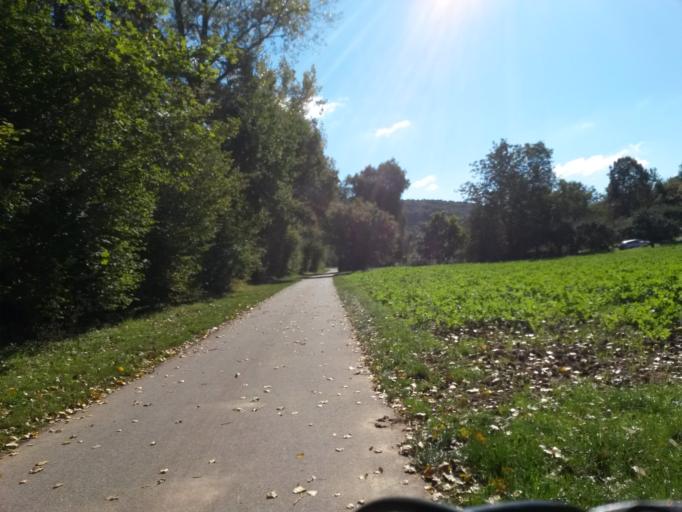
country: DE
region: Baden-Wuerttemberg
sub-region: Regierungsbezirk Stuttgart
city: Markgroningen
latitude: 48.9343
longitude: 9.0807
